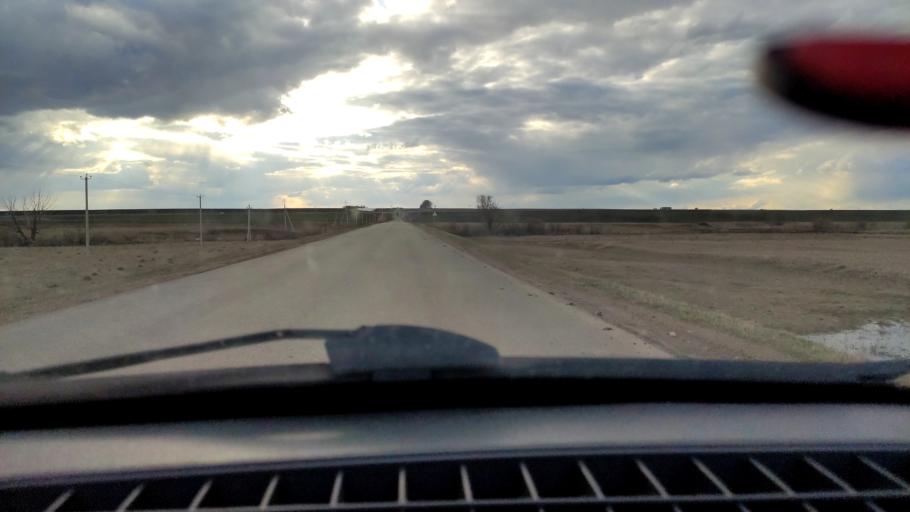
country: RU
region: Bashkortostan
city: Tolbazy
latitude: 54.2918
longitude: 55.8932
